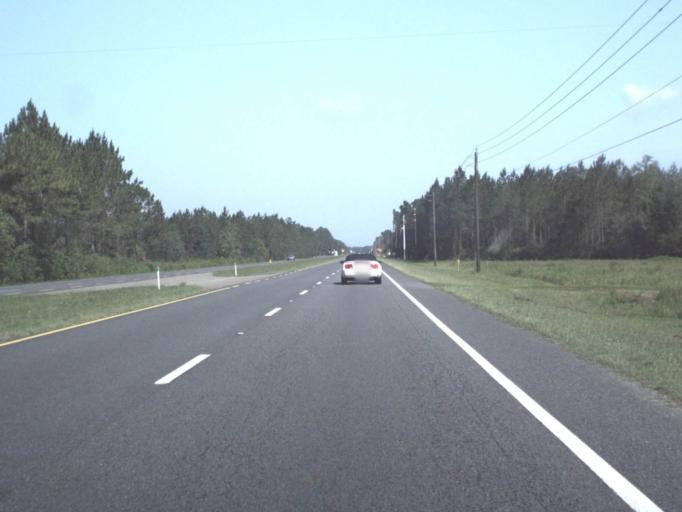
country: US
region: Florida
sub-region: Nassau County
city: Hilliard
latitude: 30.6684
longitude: -81.8929
